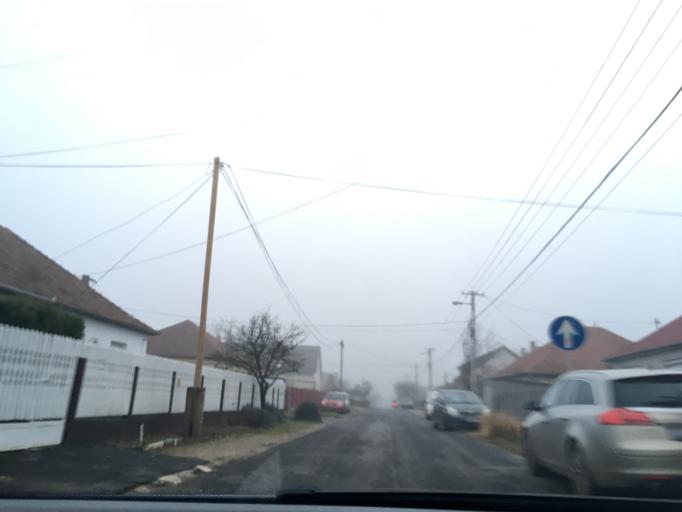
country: HU
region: Hajdu-Bihar
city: Debrecen
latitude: 47.5468
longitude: 21.6662
